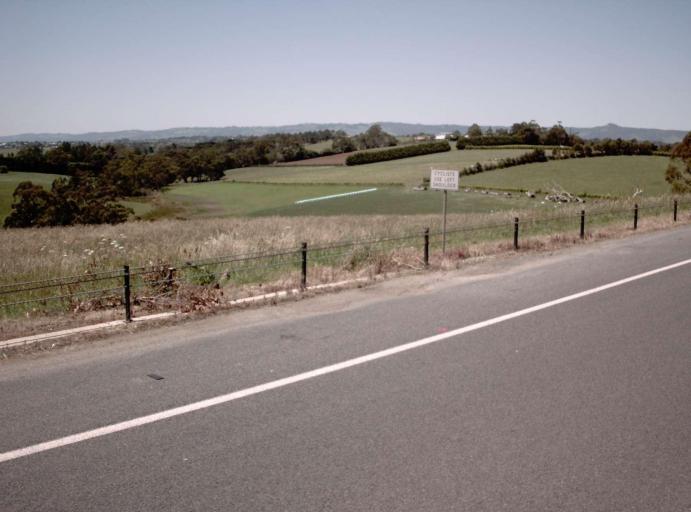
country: AU
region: Victoria
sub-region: Baw Baw
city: Warragul
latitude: -38.1430
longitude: 145.8846
